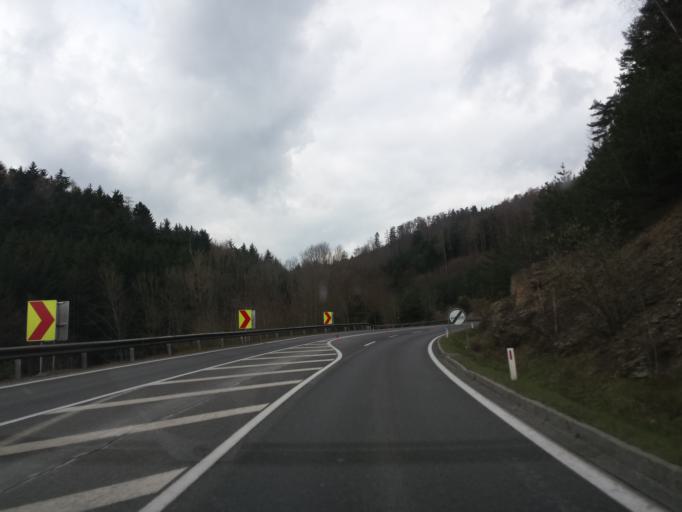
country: AT
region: Lower Austria
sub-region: Politischer Bezirk Krems
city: Lengenfeld
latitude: 48.5004
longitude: 15.5555
